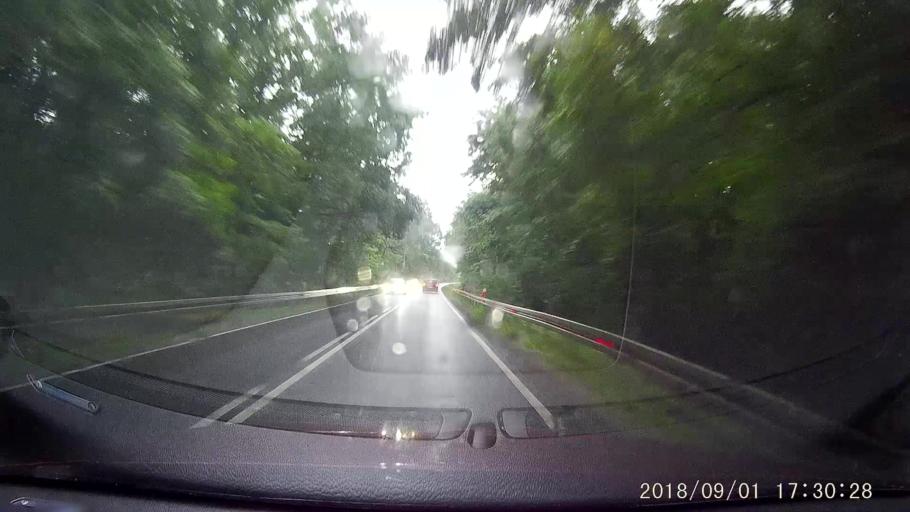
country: PL
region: Lubusz
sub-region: Powiat zaganski
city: Zagan
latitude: 51.6416
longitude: 15.3209
